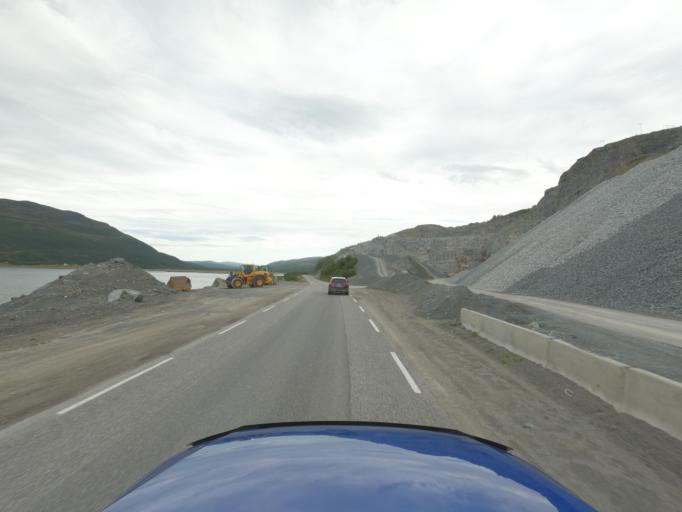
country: NO
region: Finnmark Fylke
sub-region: Kvalsund
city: Kvalsund
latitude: 70.4538
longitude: 24.2825
